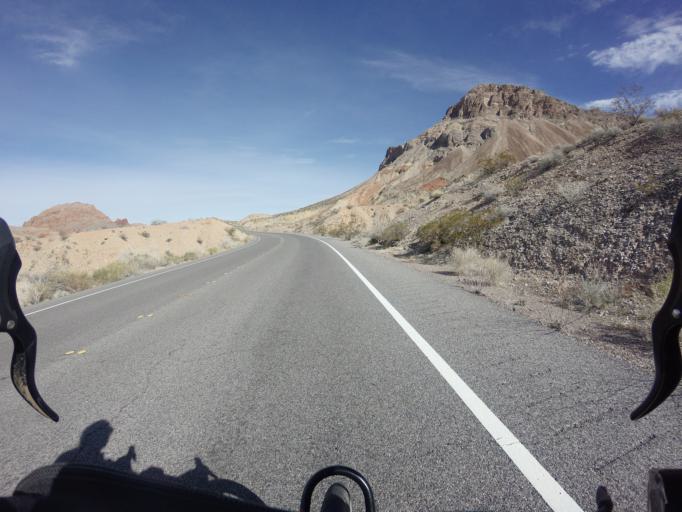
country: US
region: Nevada
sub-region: Clark County
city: Boulder City
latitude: 36.2162
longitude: -114.6361
